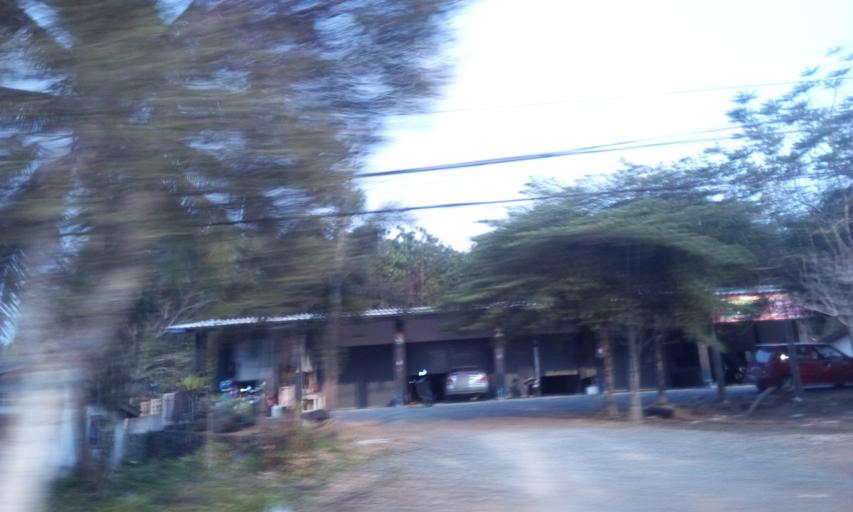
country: TH
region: Trat
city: Khao Saming
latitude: 12.3599
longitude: 102.3835
